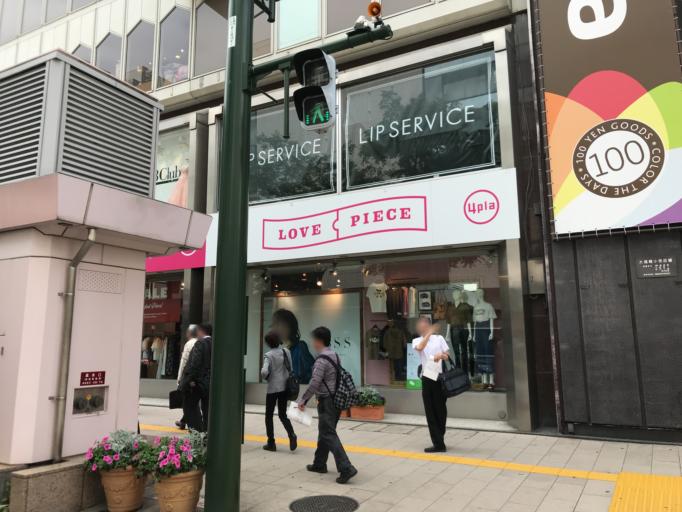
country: JP
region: Hokkaido
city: Sapporo
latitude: 43.0588
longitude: 141.3525
